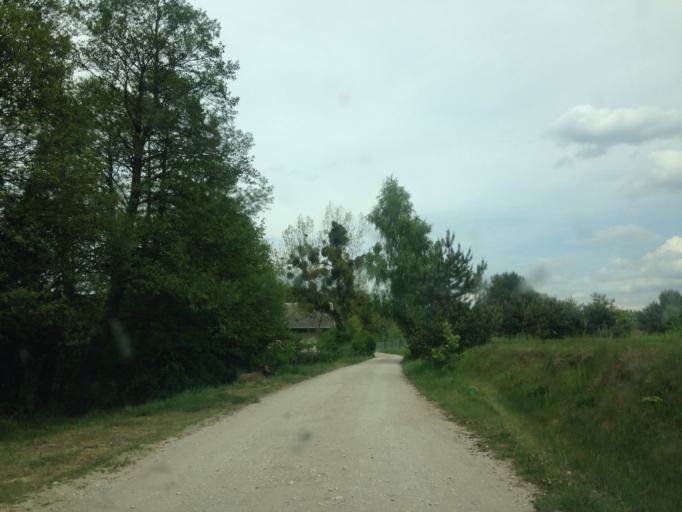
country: PL
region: Kujawsko-Pomorskie
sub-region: Powiat brodnicki
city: Brodnica
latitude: 53.3245
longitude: 19.3585
